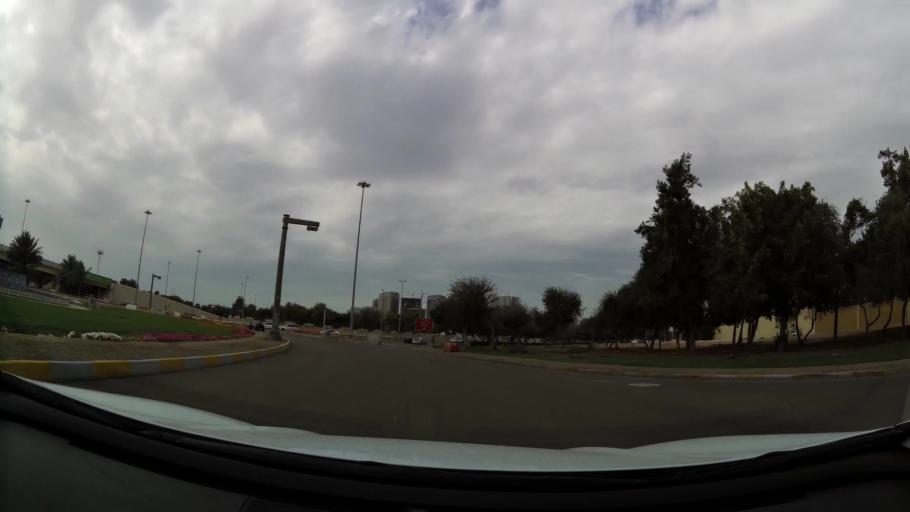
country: AE
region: Abu Dhabi
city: Abu Dhabi
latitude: 24.4272
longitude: 54.4453
